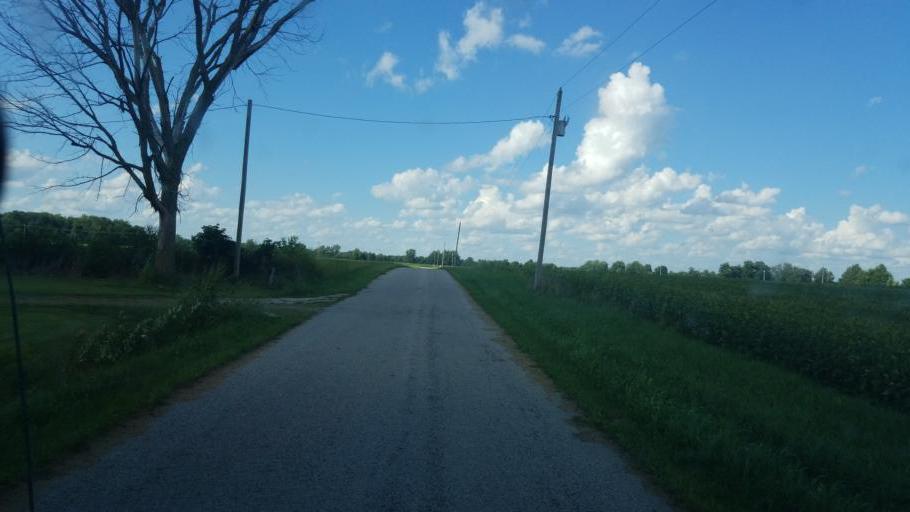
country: US
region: Ohio
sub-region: Union County
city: Richwood
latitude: 40.5442
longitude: -83.3767
